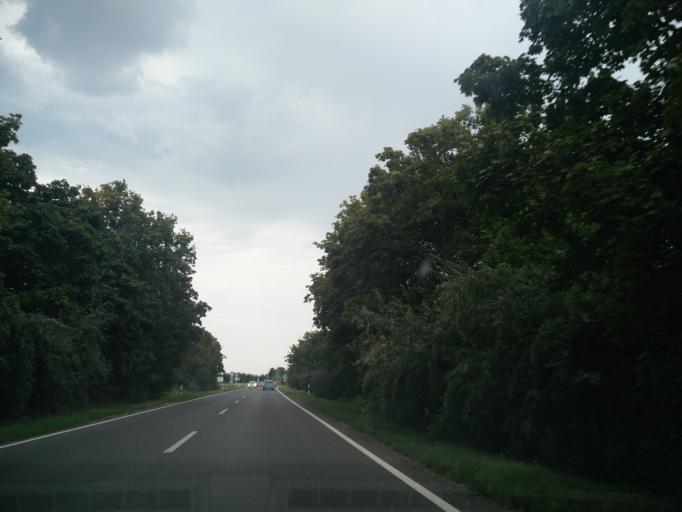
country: HU
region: Fejer
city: Polgardi
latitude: 47.0653
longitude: 18.3099
